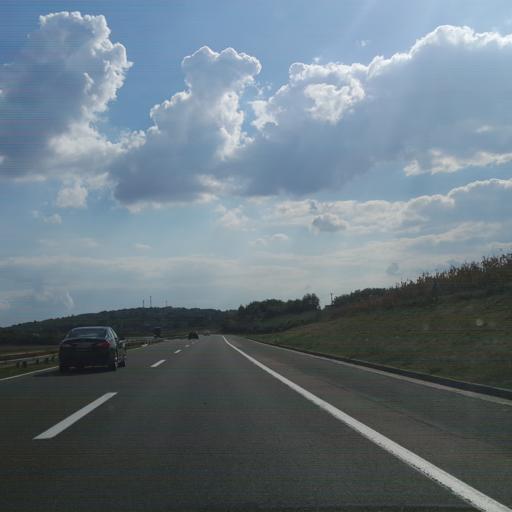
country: RS
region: Central Serbia
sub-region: Podunavski Okrug
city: Velika Plana
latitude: 44.4193
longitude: 21.0571
